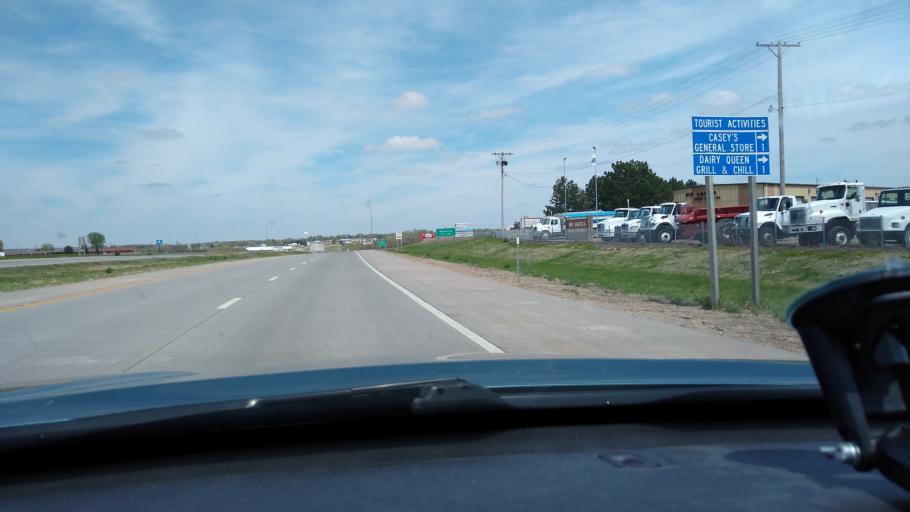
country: US
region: Kansas
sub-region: Republic County
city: Belleville
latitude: 39.8084
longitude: -97.6492
